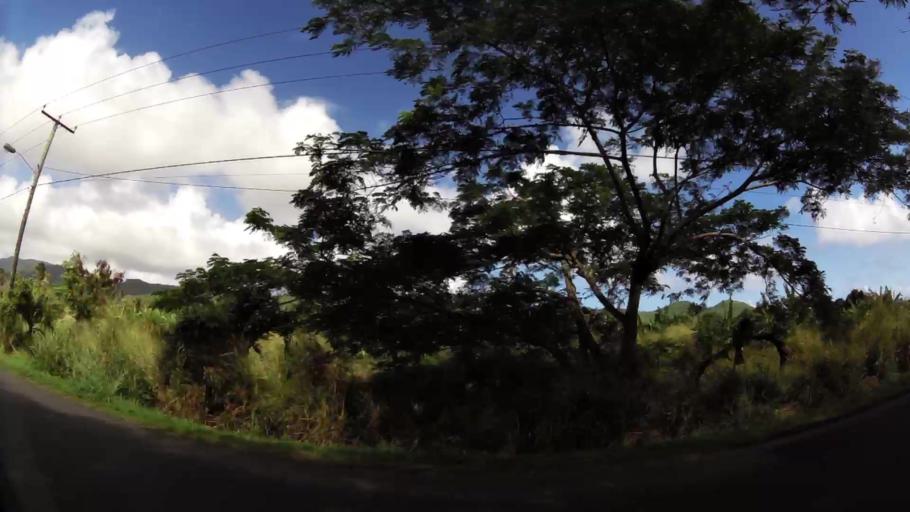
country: LC
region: Dennery Quarter
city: Dennery
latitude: 13.9281
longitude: -60.8996
